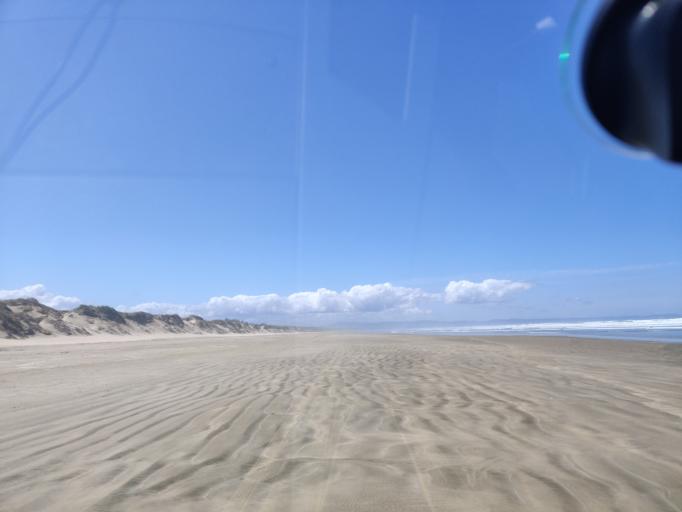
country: NZ
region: Northland
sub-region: Far North District
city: Kaitaia
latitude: -34.9759
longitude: 173.1380
